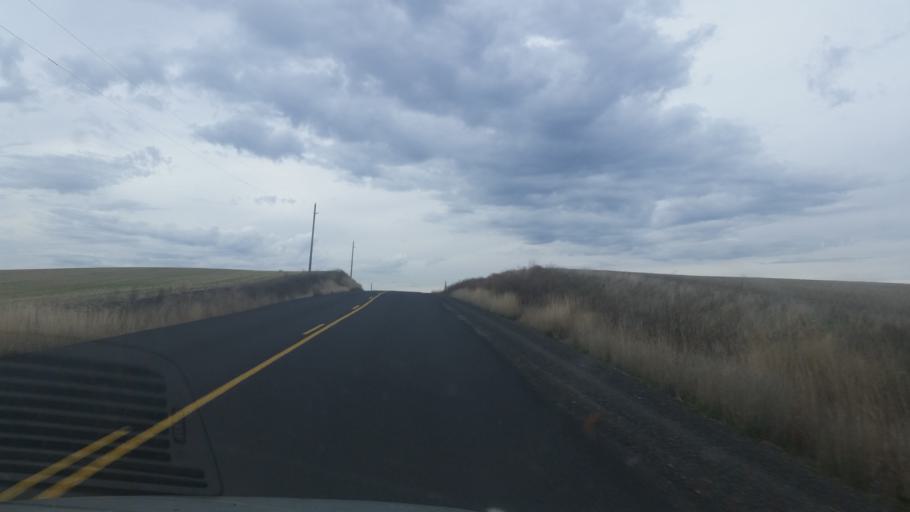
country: US
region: Washington
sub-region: Spokane County
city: Cheney
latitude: 47.3906
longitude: -117.4601
